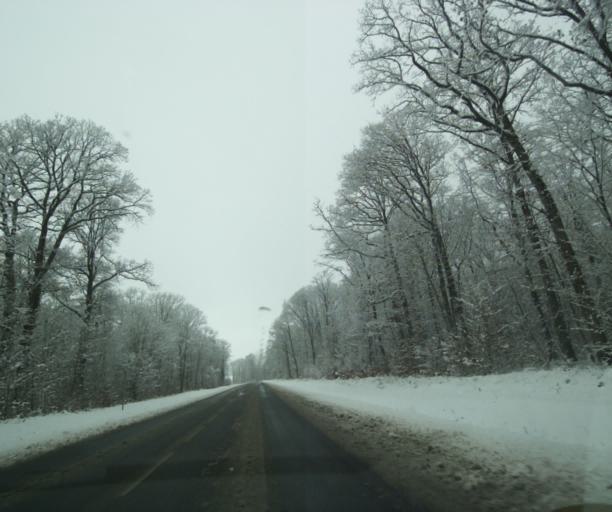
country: FR
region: Champagne-Ardenne
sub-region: Departement de la Haute-Marne
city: Montier-en-Der
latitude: 48.5422
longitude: 4.8280
